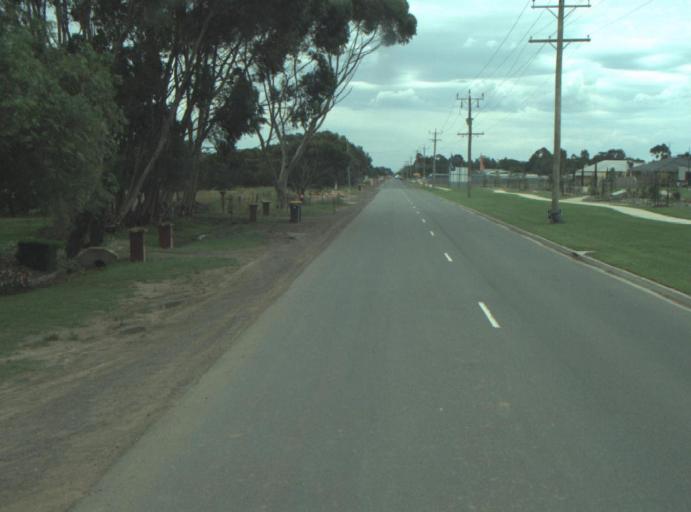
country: AU
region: Victoria
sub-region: Greater Geelong
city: Leopold
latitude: -38.1985
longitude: 144.4532
